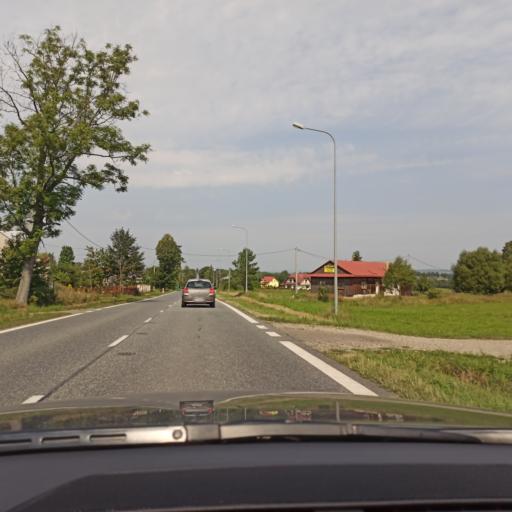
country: PL
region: Subcarpathian Voivodeship
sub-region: Powiat jasielski
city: Nowy Zmigrod
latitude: 49.5927
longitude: 21.5384
